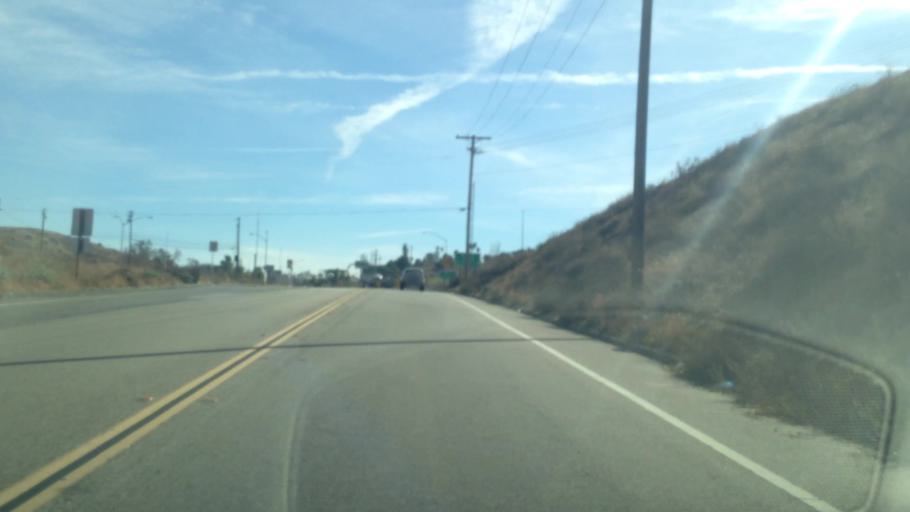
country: US
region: California
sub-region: Riverside County
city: Highgrove
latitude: 33.9616
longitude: -117.3113
